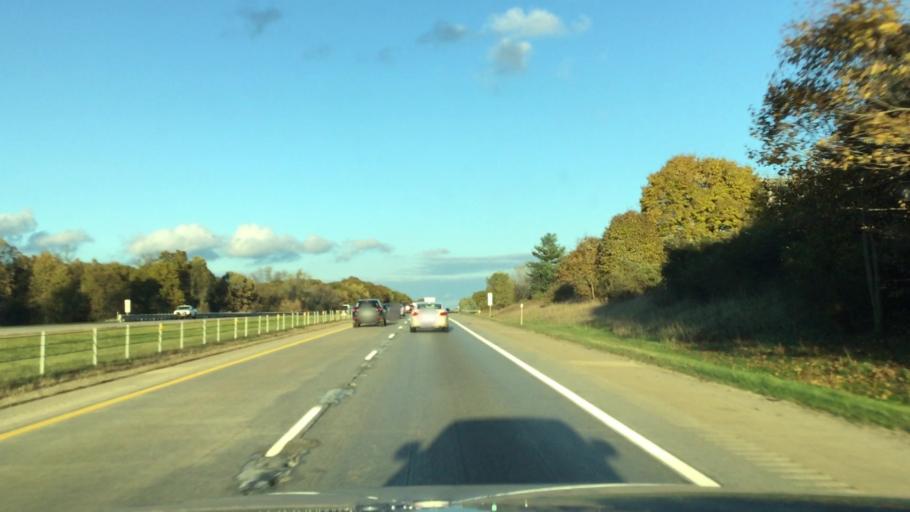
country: US
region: Michigan
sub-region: Calhoun County
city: Brownlee Park
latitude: 42.2928
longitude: -85.1056
